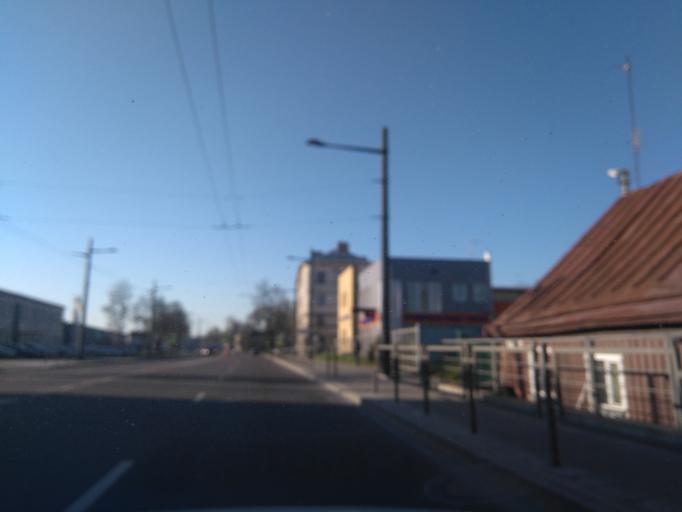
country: LT
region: Kauno apskritis
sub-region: Kaunas
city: Aleksotas
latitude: 54.8778
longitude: 23.9341
